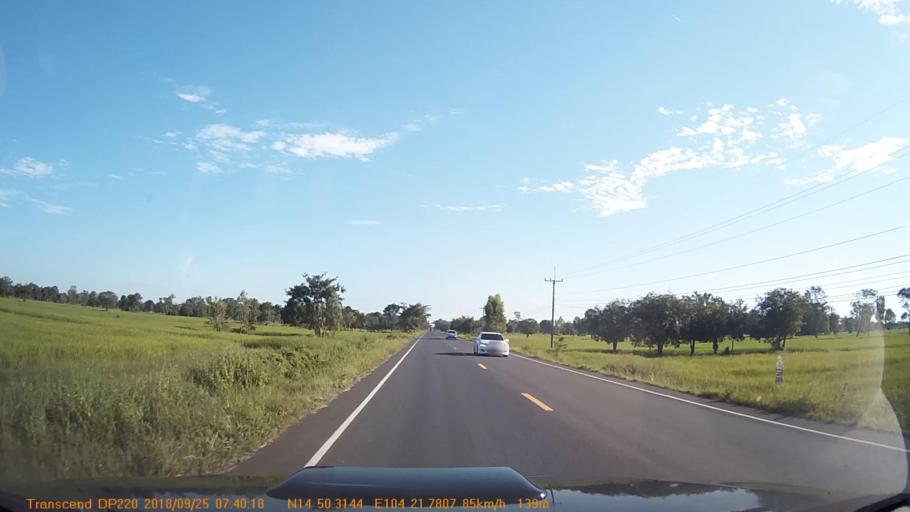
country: TH
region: Sisaket
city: Phayu
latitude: 14.8392
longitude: 104.3632
